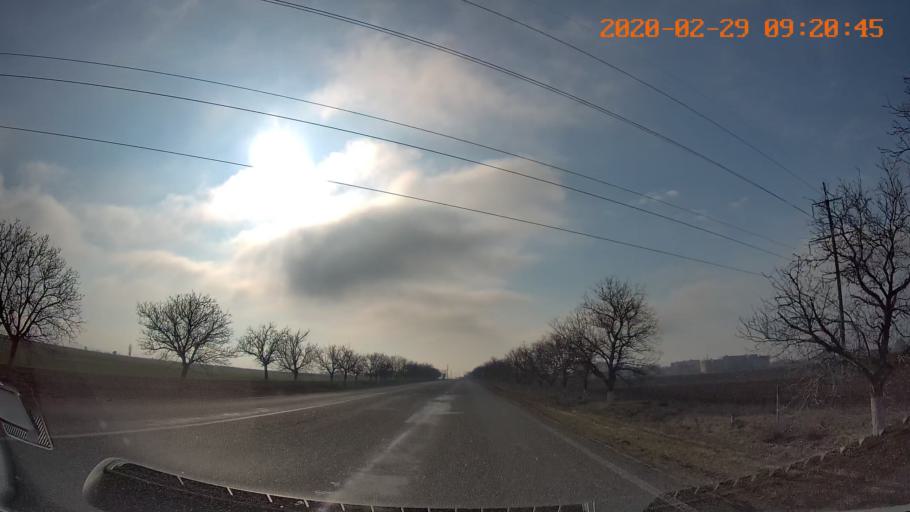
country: MD
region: Telenesti
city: Pervomaisc
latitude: 46.7442
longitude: 29.9526
